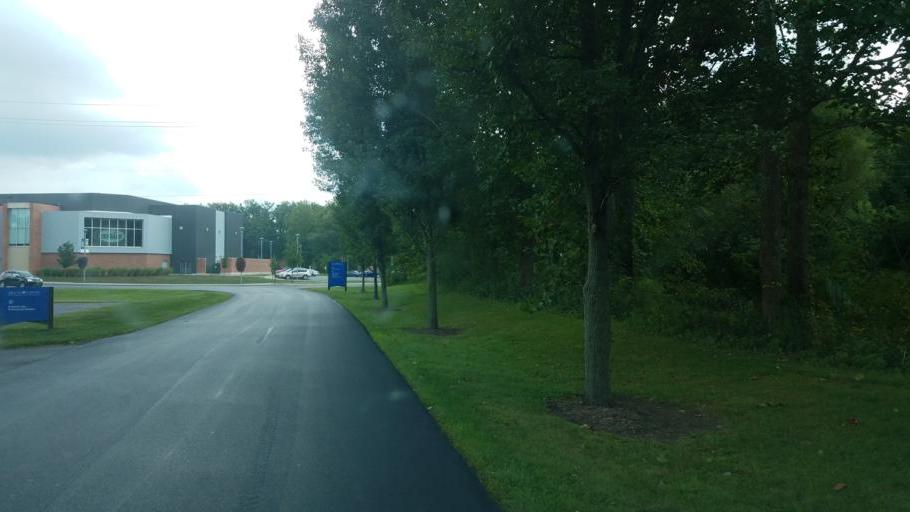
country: US
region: Ohio
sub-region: Knox County
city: Mount Vernon
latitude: 40.3719
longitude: -82.4700
